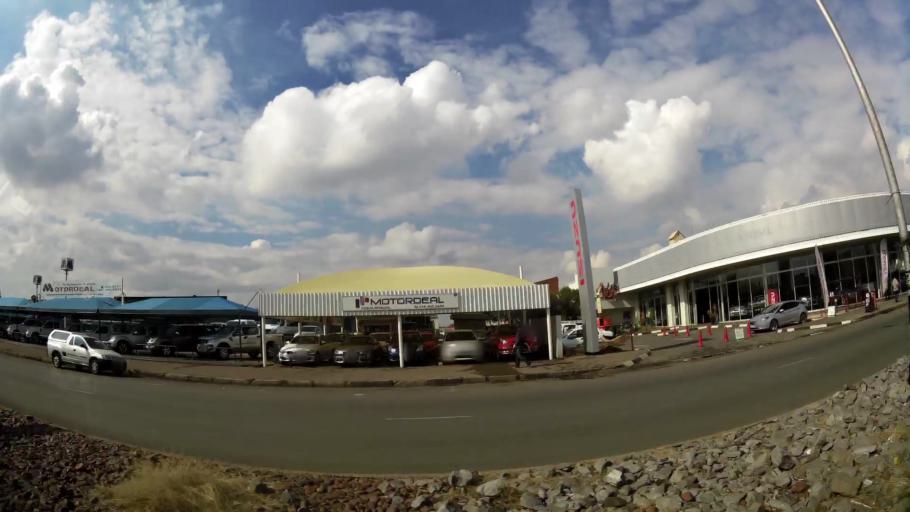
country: ZA
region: Gauteng
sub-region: Sedibeng District Municipality
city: Vereeniging
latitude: -26.6689
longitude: 27.9329
